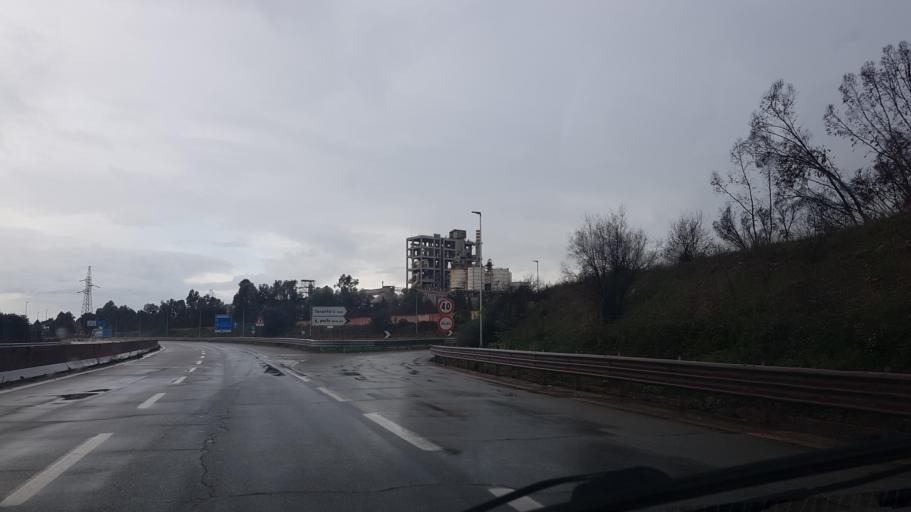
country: IT
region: Apulia
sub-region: Provincia di Taranto
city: Statte
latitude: 40.4899
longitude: 17.2105
